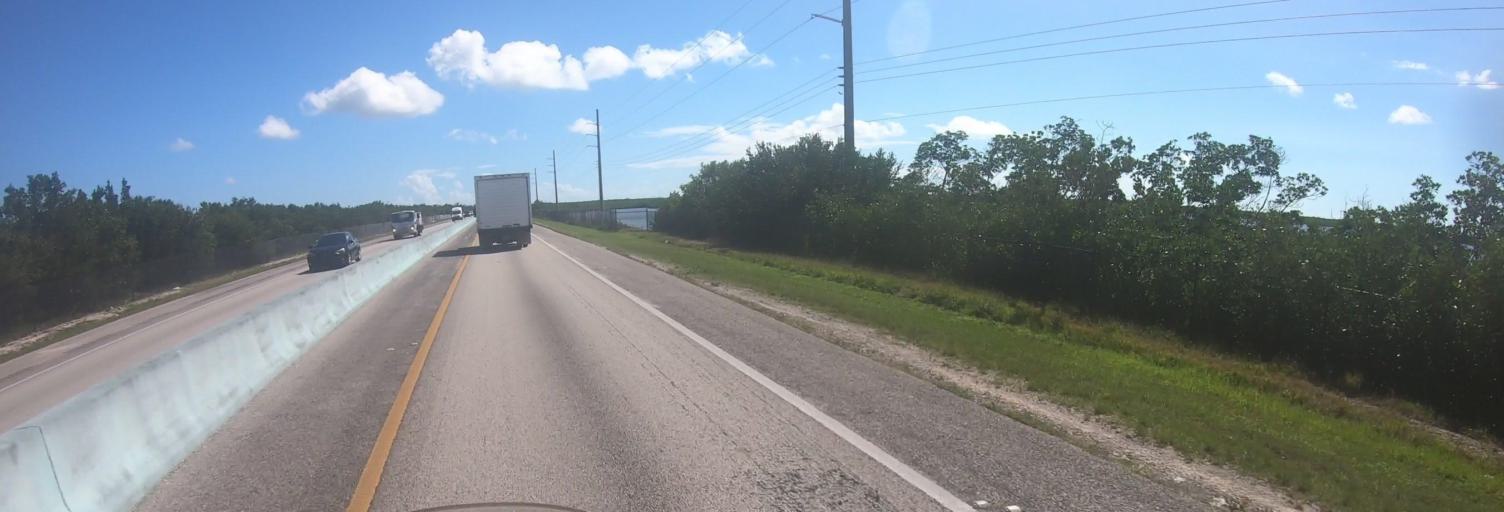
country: US
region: Florida
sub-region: Monroe County
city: North Key Largo
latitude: 25.2504
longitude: -80.4365
